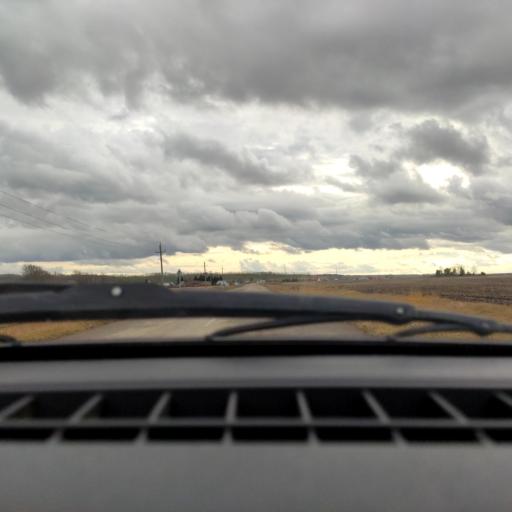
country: RU
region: Bashkortostan
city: Asanovo
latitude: 54.9323
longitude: 55.5176
